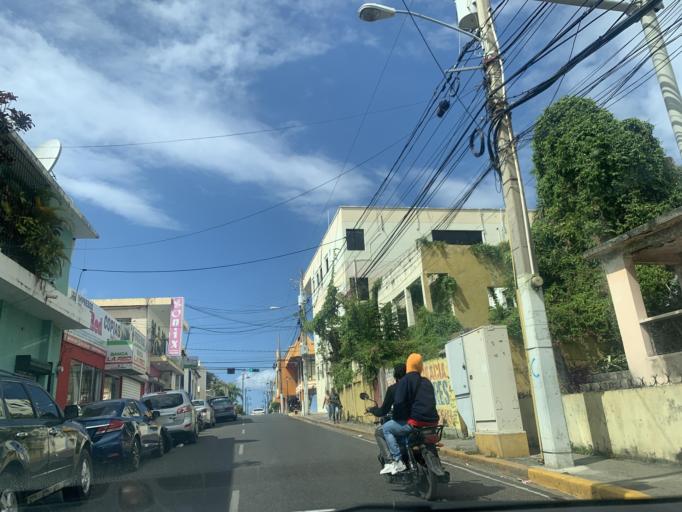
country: DO
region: Puerto Plata
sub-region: Puerto Plata
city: Puerto Plata
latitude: 19.7962
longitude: -70.6939
